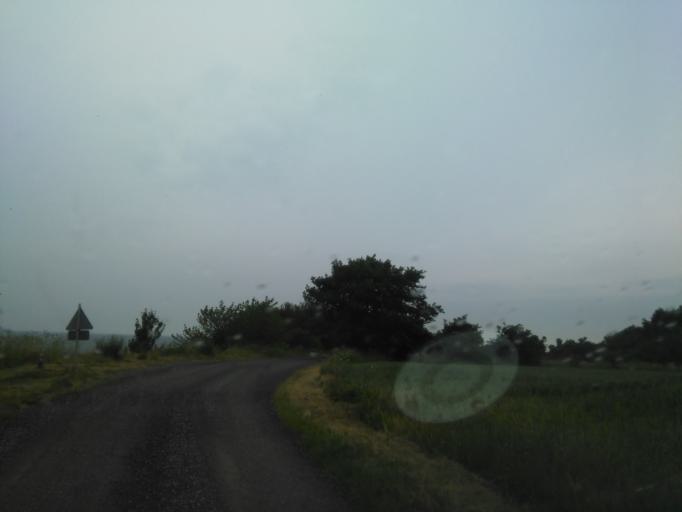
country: DK
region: Capital Region
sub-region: Bornholm Kommune
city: Akirkeby
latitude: 55.0423
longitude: 14.8330
